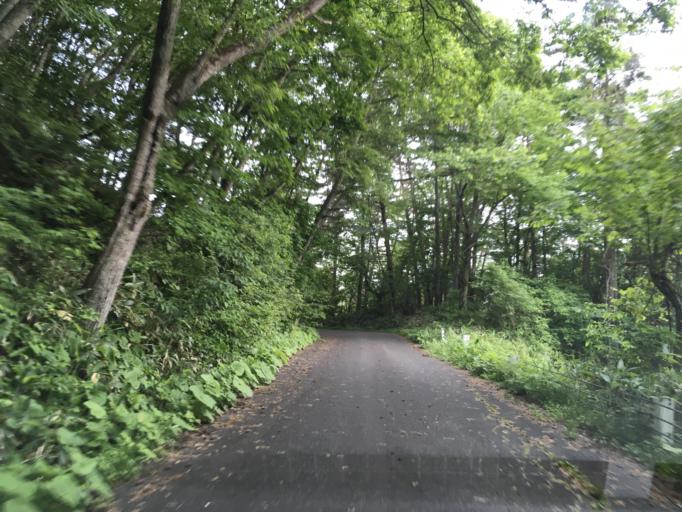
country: JP
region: Iwate
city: Mizusawa
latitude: 39.1304
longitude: 141.2982
